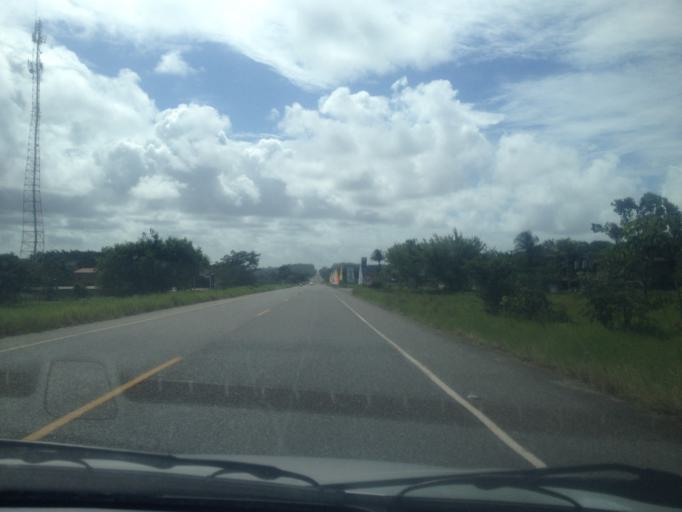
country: BR
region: Bahia
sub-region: Entre Rios
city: Entre Rios
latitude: -12.3035
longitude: -37.9015
